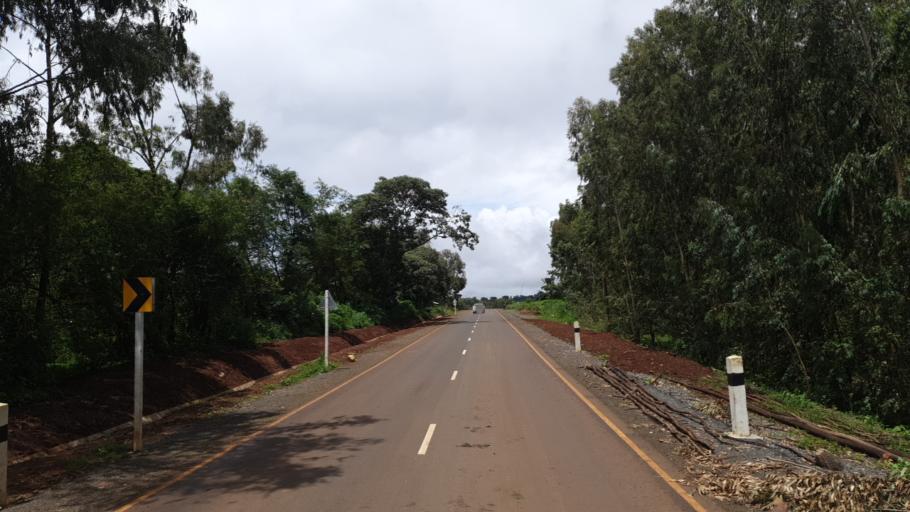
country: ET
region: Oromiya
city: Shambu
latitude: 9.9531
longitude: 36.8362
